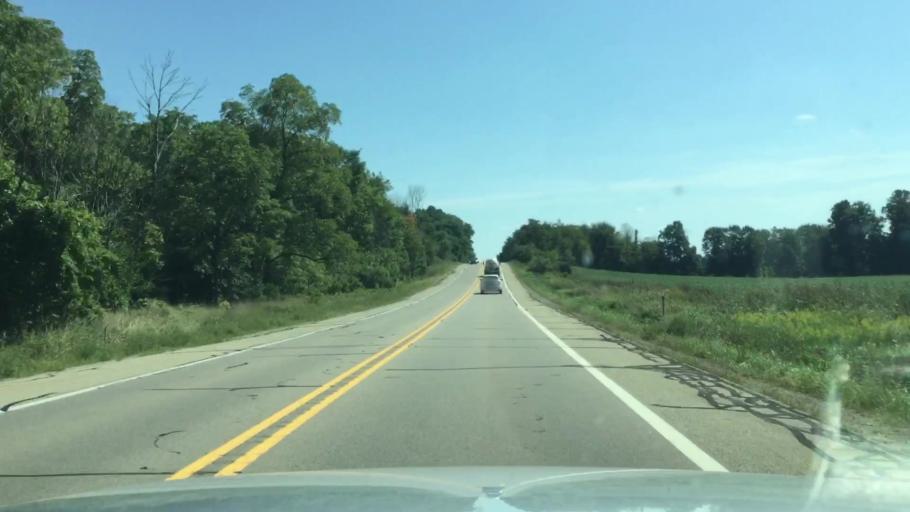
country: US
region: Michigan
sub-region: Lenawee County
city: Clinton
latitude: 42.0731
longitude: -84.0240
